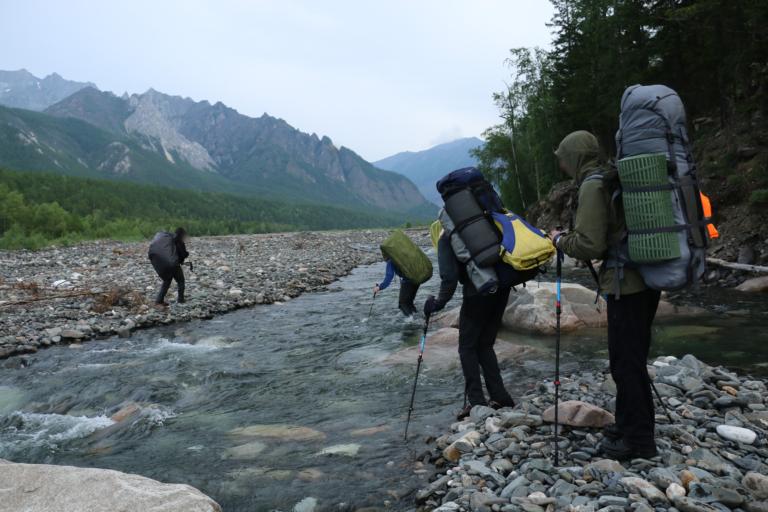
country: RU
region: Respublika Buryatiya
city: Novyy Uoyan
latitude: 56.2229
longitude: 111.5067
